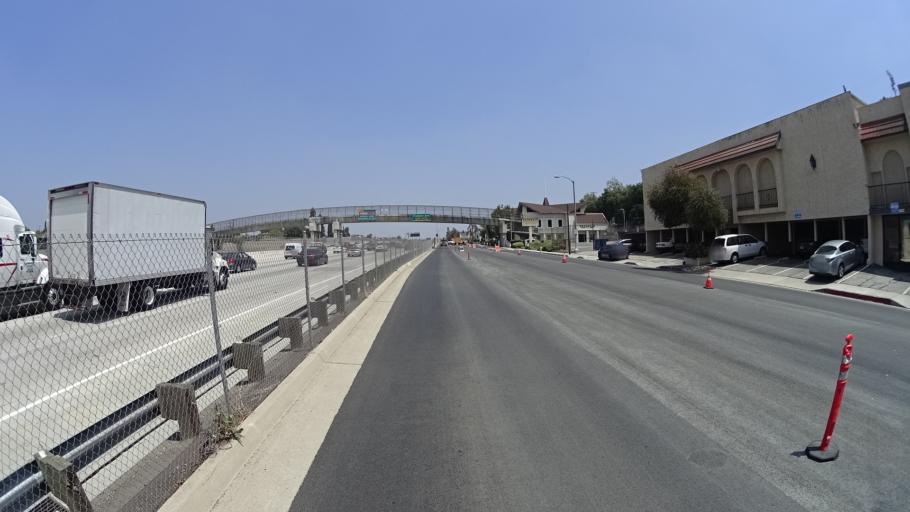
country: US
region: California
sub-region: Los Angeles County
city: Belvedere
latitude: 34.0640
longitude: -118.1588
